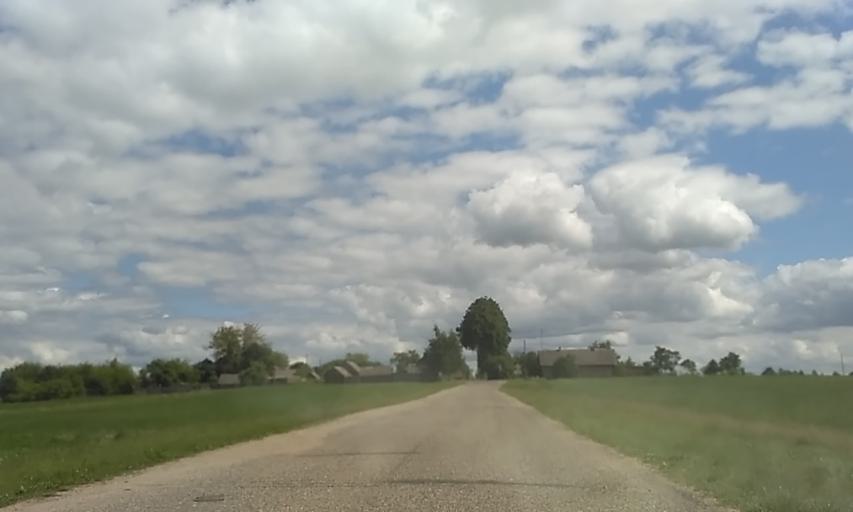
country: BY
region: Minsk
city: Krupki
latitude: 54.3499
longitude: 29.1267
